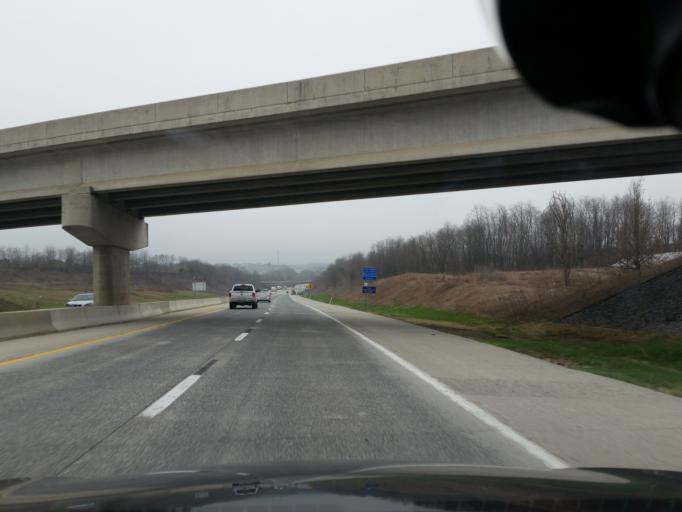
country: US
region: Pennsylvania
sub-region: Cumberland County
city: Shiremanstown
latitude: 40.2443
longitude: -76.9815
